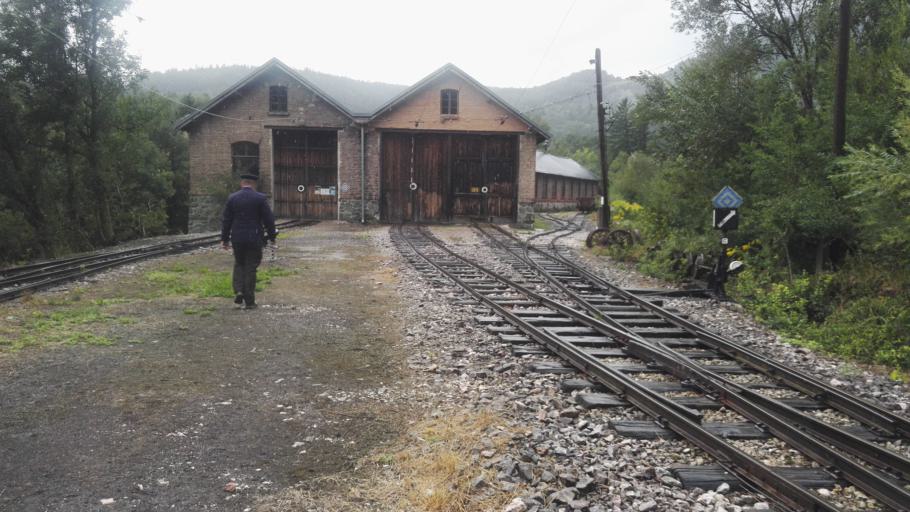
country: AT
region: Lower Austria
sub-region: Politischer Bezirk Neunkirchen
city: Reichenau an der Rax
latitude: 47.7064
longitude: 15.8162
